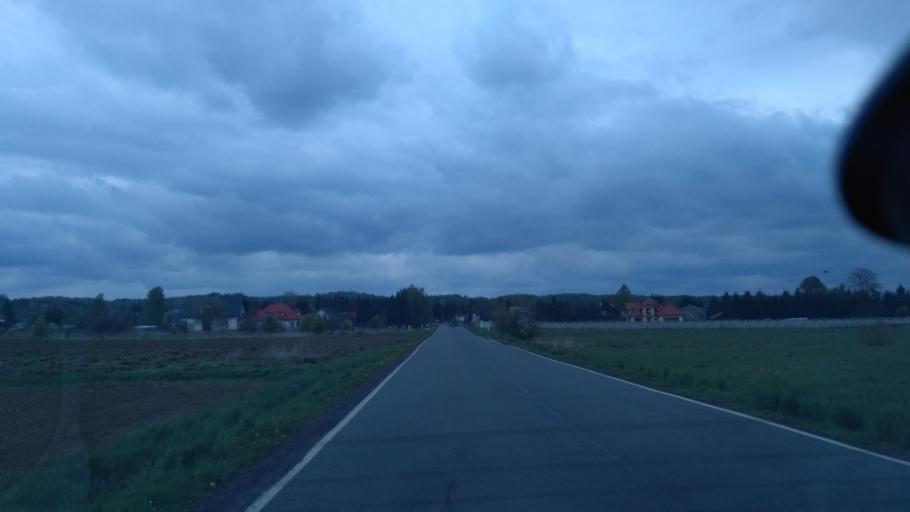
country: PL
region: Subcarpathian Voivodeship
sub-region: Powiat brzozowski
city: Jasionow
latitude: 49.6563
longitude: 21.9908
